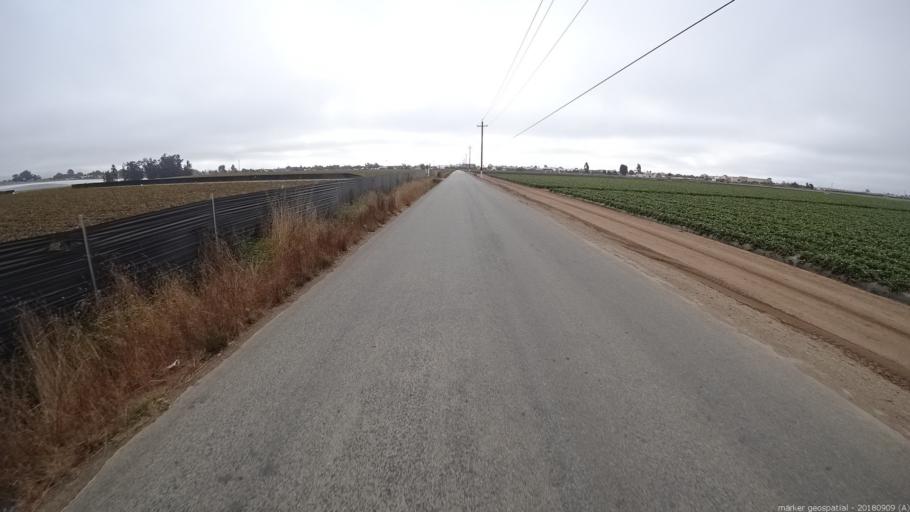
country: US
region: California
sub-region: Monterey County
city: Boronda
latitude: 36.7253
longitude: -121.6700
